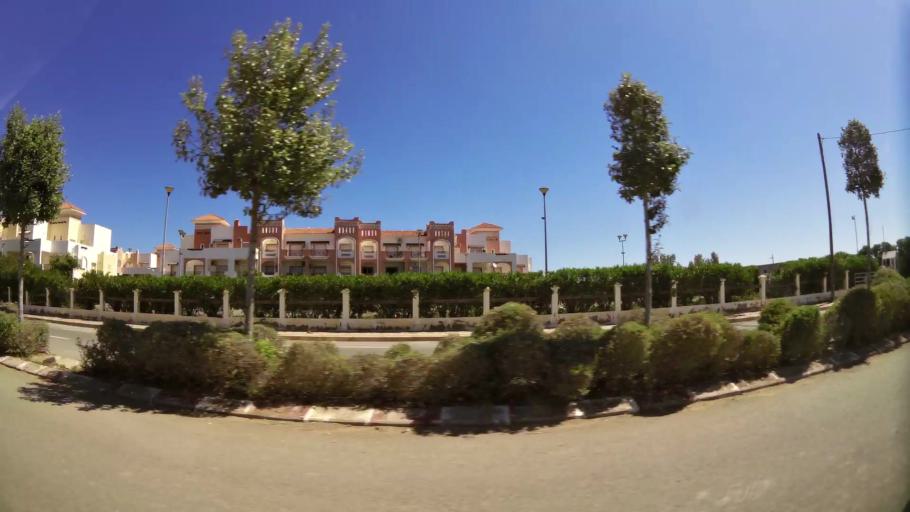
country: MA
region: Oriental
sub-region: Berkane-Taourirt
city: Madagh
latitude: 35.1030
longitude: -2.3128
